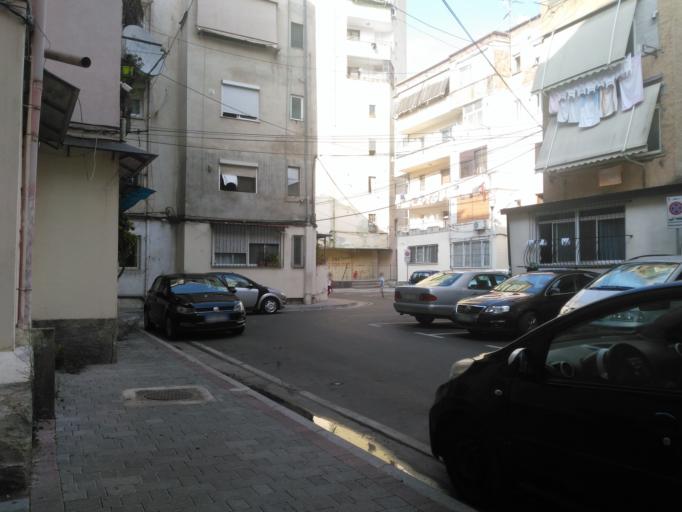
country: AL
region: Tirane
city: Tirana
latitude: 41.3173
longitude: 19.8094
